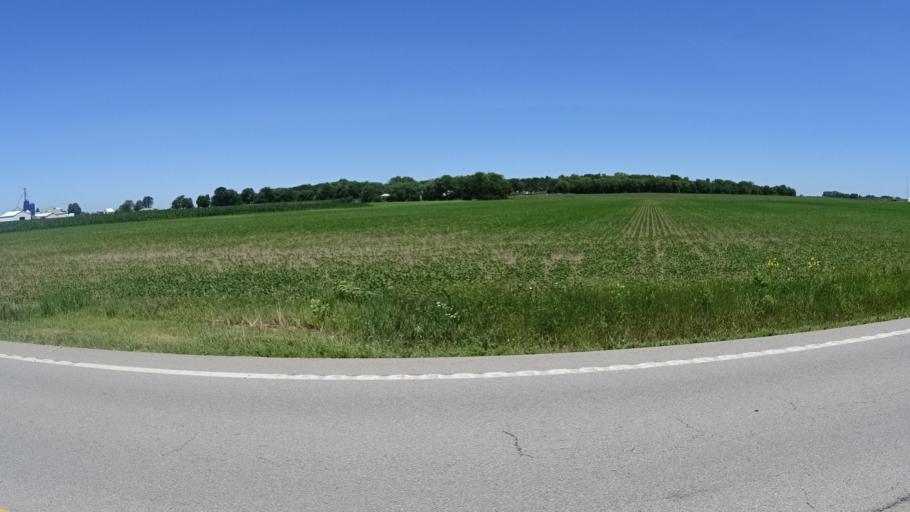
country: US
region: Ohio
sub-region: Ottawa County
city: Port Clinton
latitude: 41.4329
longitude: -82.8408
